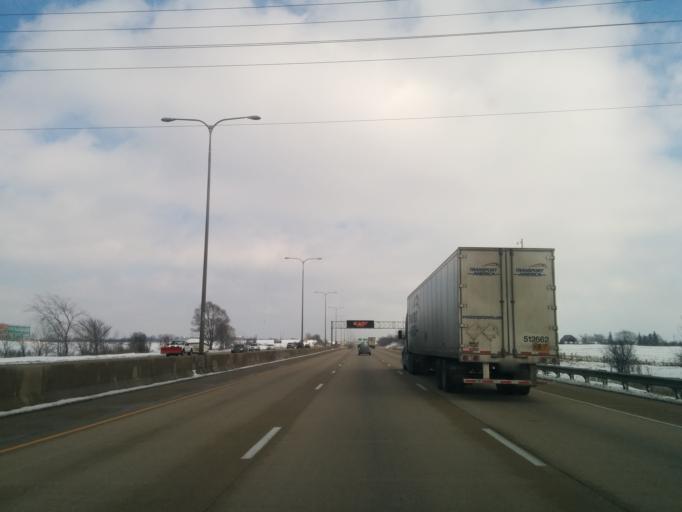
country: US
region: Illinois
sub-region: Will County
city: Mokena
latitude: 41.5526
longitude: -87.8710
